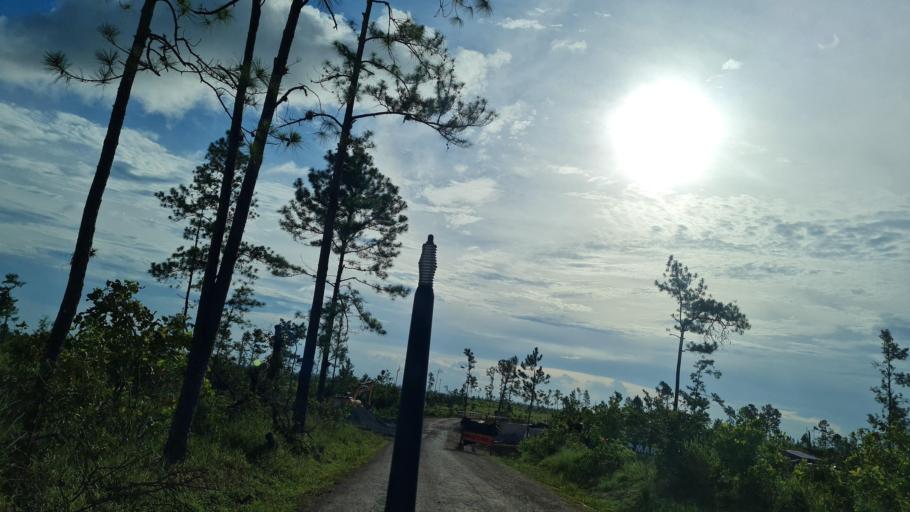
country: NI
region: Atlantico Sur
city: La Cruz de Rio Grande
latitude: 13.5271
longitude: -84.2536
